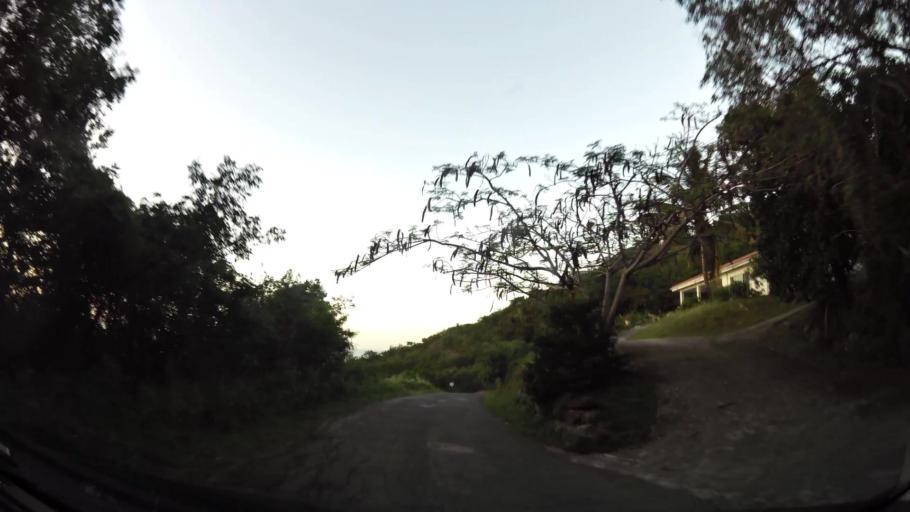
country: VG
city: Tortola
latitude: 18.4494
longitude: -64.5768
